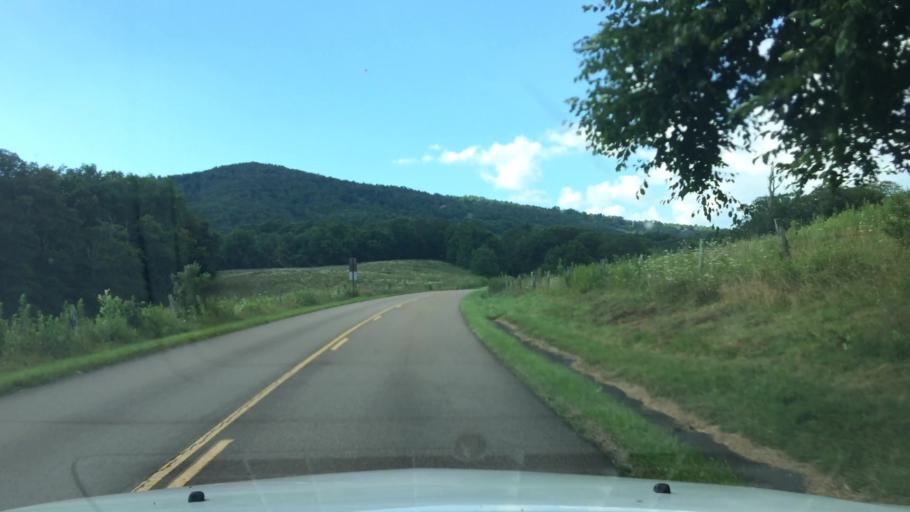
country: US
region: North Carolina
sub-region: Watauga County
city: Blowing Rock
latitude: 36.1506
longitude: -81.6660
